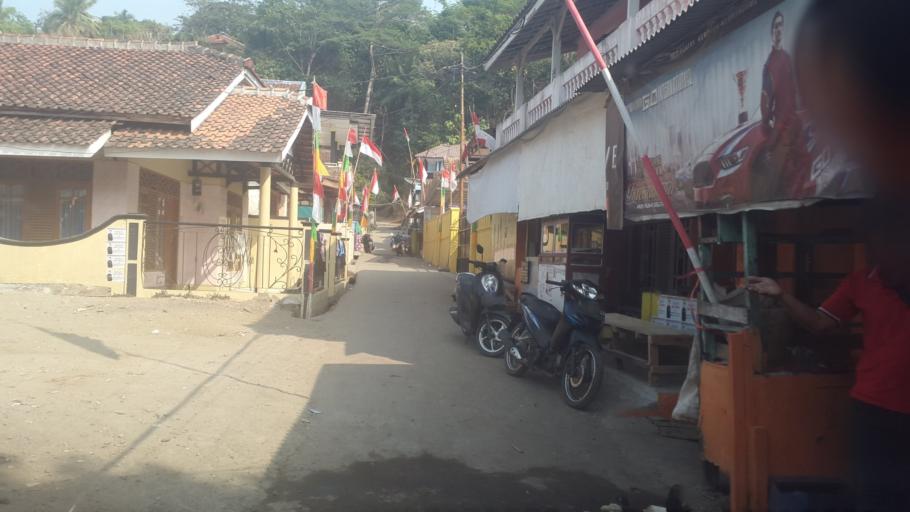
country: ID
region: West Java
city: Tugu
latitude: -6.9515
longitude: 106.4399
